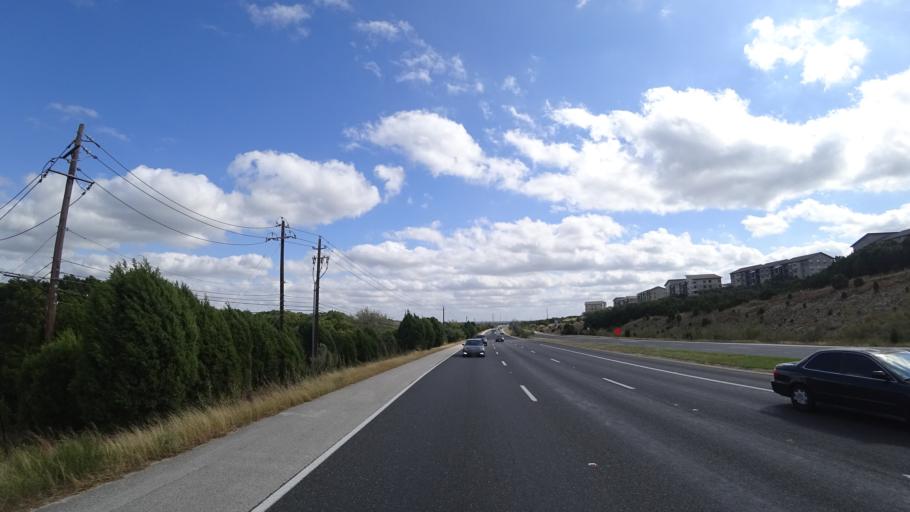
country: US
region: Texas
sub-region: Travis County
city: Barton Creek
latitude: 30.2518
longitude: -97.8584
